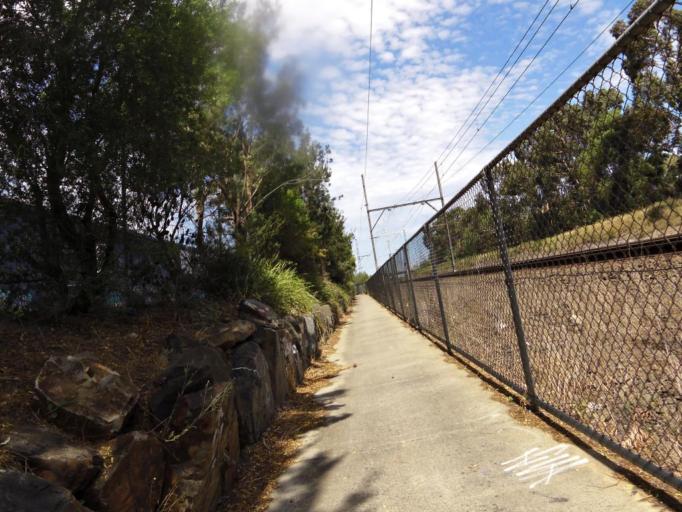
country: AU
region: Victoria
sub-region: Monash
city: Oakleigh South
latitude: -37.9092
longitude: 145.1001
